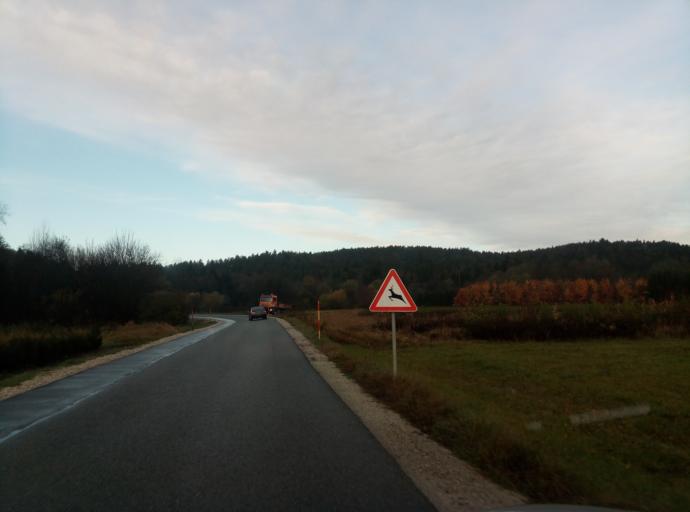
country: SI
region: Menges
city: Menges
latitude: 46.1721
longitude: 14.5597
